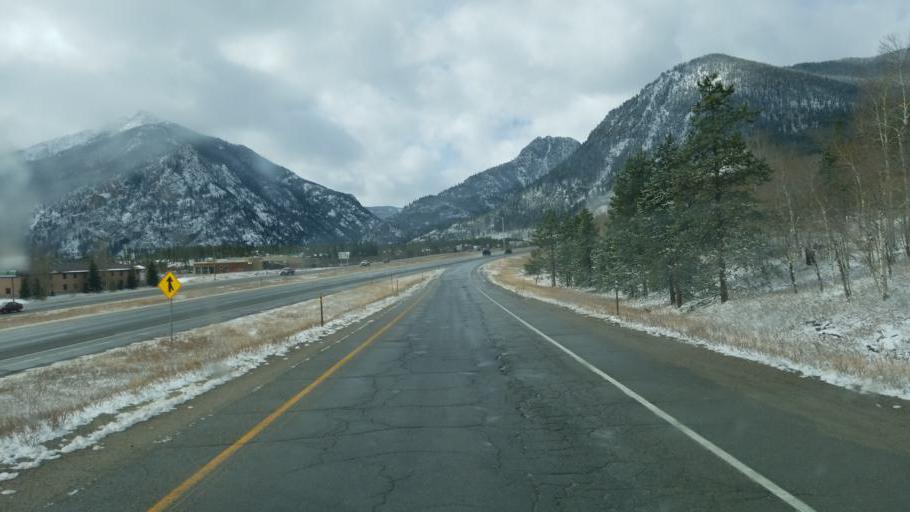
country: US
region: Colorado
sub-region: Summit County
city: Frisco
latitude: 39.5921
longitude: -106.0982
